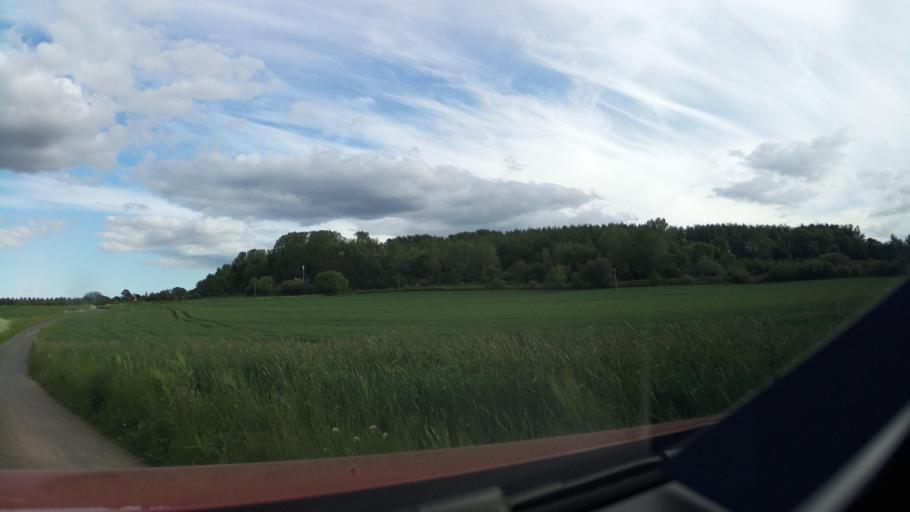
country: GB
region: England
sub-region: Gloucestershire
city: Moreton in Marsh
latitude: 52.0258
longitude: -1.7147
